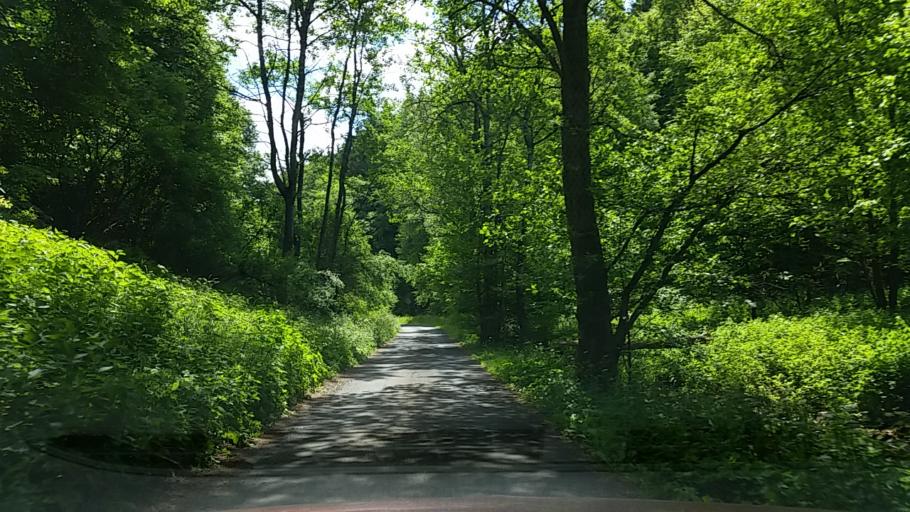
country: DE
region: Bavaria
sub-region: Regierungsbezirk Unterfranken
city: Neuendorf
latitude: 50.0271
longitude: 9.6578
